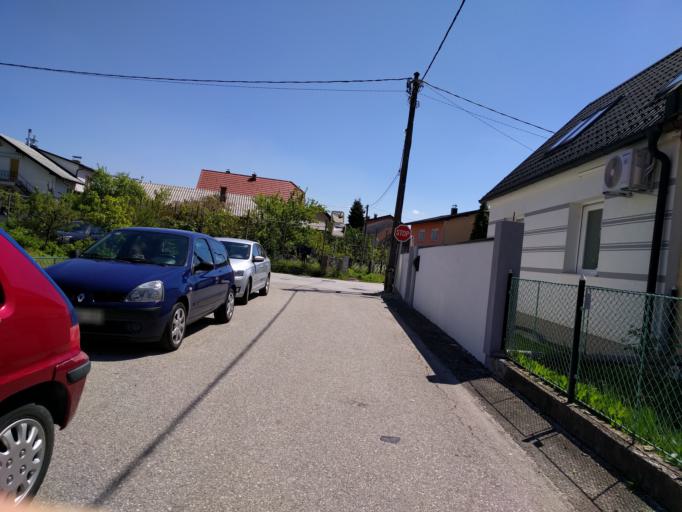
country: SI
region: Maribor
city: Maribor
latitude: 46.5449
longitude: 15.6707
